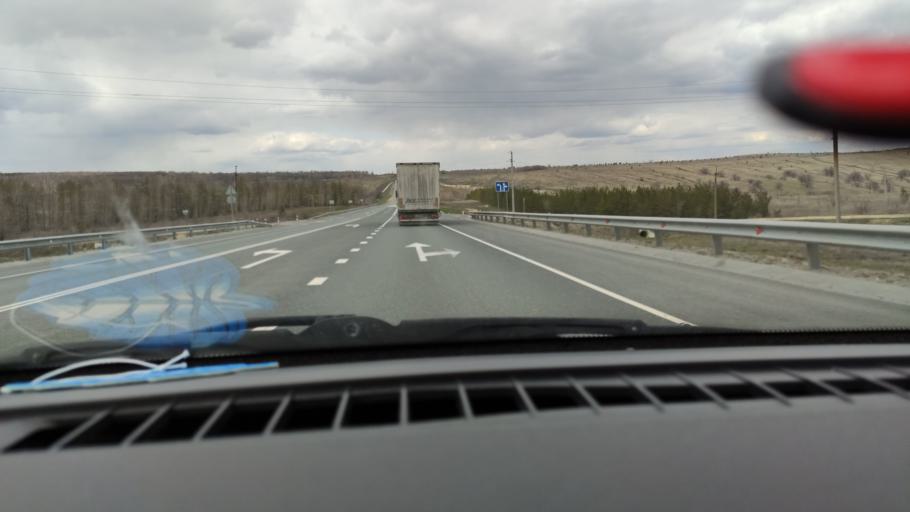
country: RU
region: Saratov
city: Shikhany
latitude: 52.1380
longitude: 47.2137
